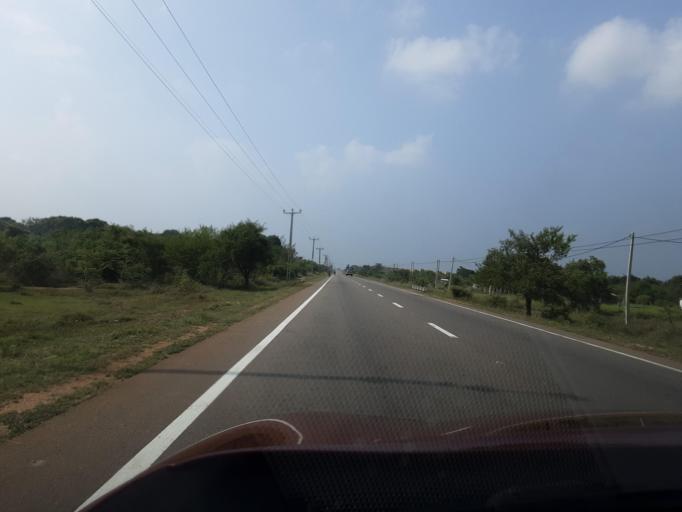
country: LK
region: Northern Province
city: Kilinochchi
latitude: 9.0823
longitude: 80.4805
